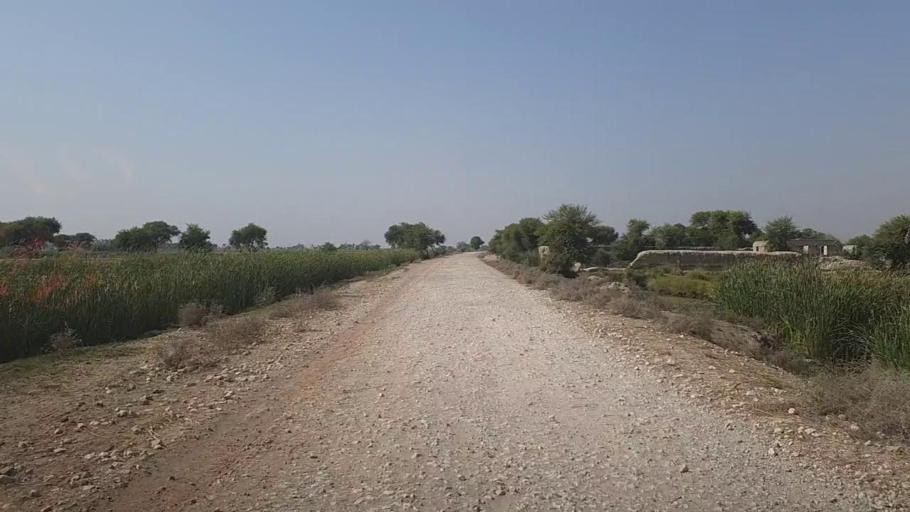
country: PK
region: Sindh
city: Kandhkot
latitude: 28.3938
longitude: 69.2775
